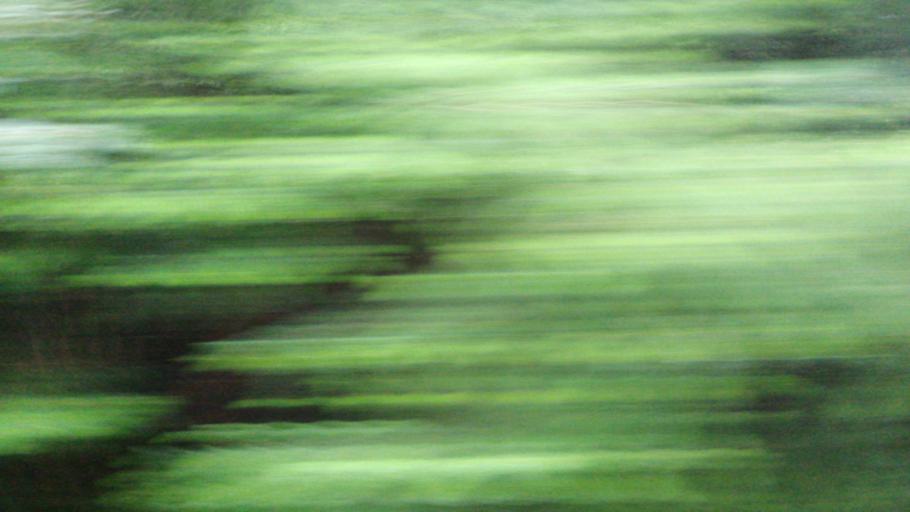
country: GB
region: Scotland
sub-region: Argyll and Bute
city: Isle Of Mull
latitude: 56.5108
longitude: -5.8017
